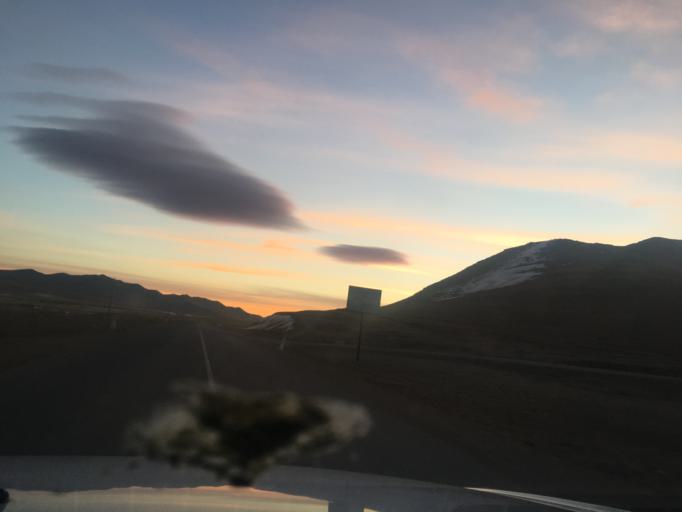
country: MN
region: Central Aimak
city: Mandal
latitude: 48.1199
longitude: 106.6479
